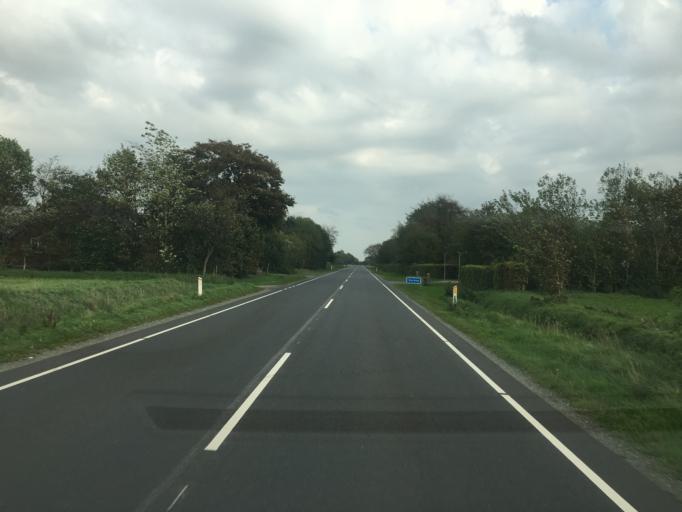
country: DK
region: South Denmark
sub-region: Tonder Kommune
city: Logumkloster
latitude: 54.9784
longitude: 9.0339
